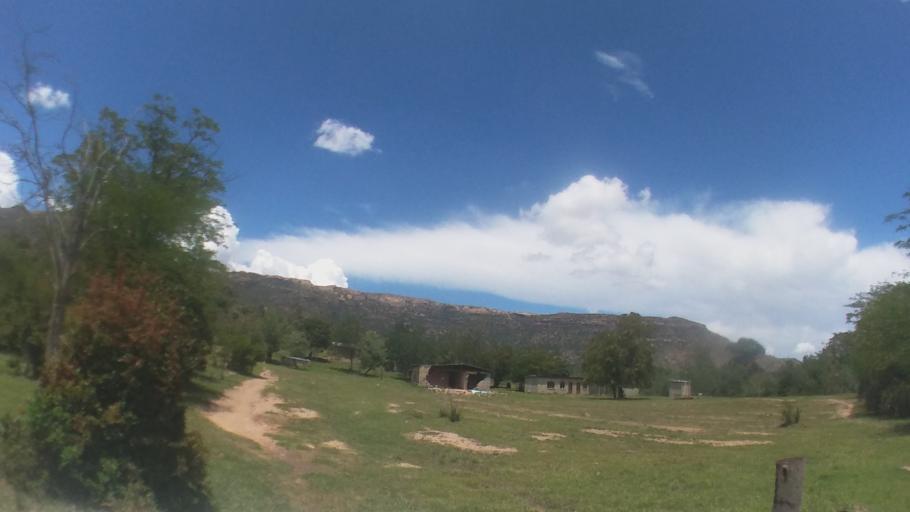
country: LS
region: Maseru
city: Nako
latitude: -29.6215
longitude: 27.5093
